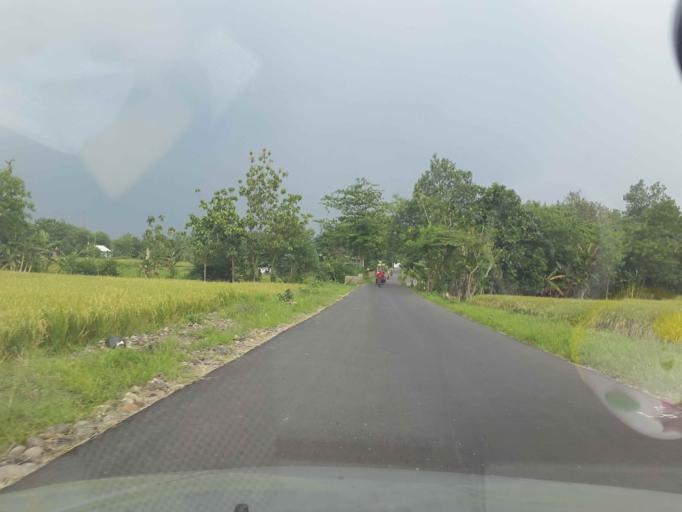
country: ID
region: Central Java
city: Jaten
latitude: -7.5626
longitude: 110.9401
